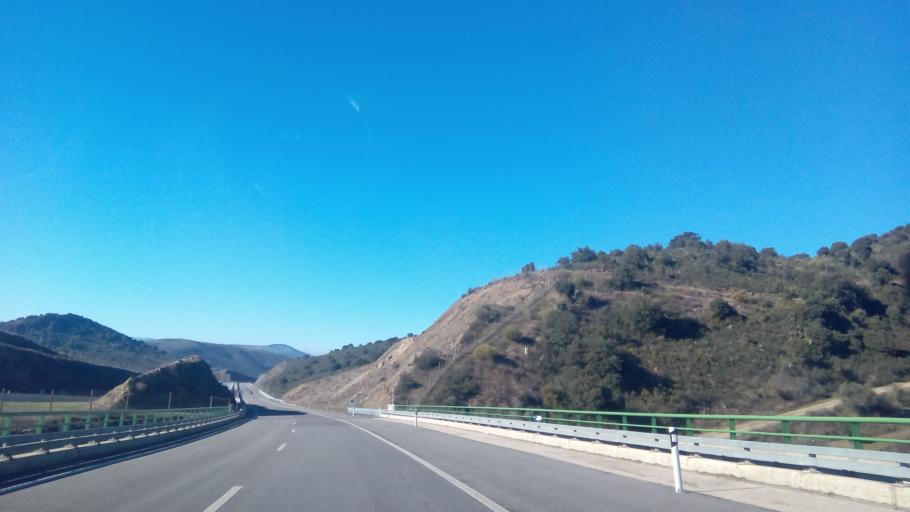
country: PT
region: Braganca
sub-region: Braganca Municipality
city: Braganca
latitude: 41.7689
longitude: -6.6607
